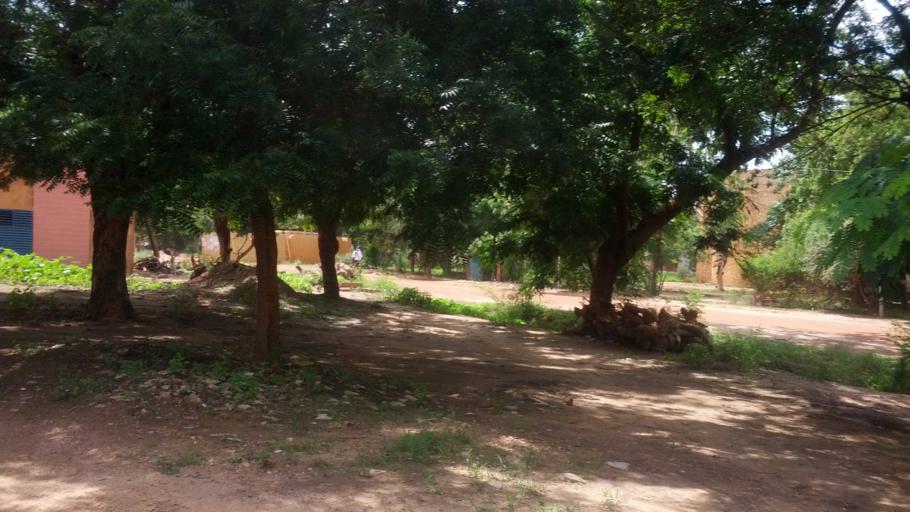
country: BF
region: Centre
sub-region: Kadiogo Province
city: Ouagadougou
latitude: 12.3778
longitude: -1.5026
